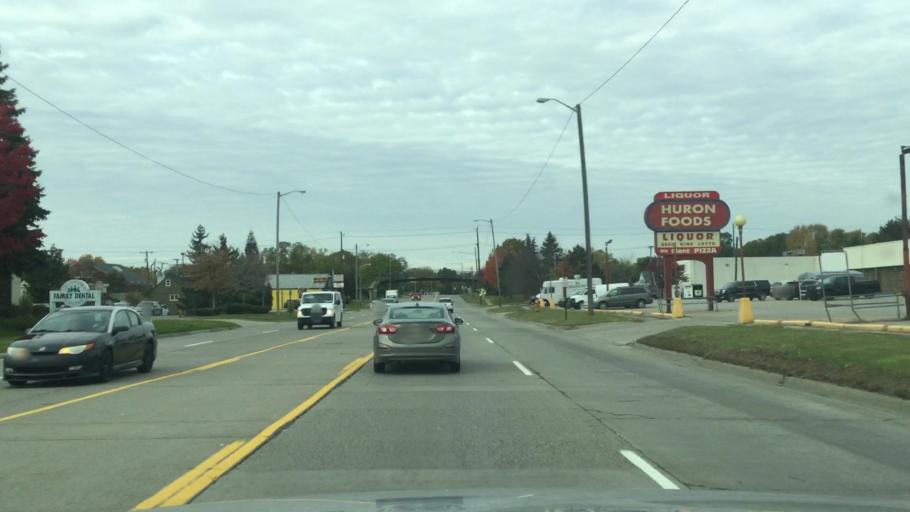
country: US
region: Michigan
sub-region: Oakland County
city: Sylvan Lake
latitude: 42.6350
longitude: -83.3332
